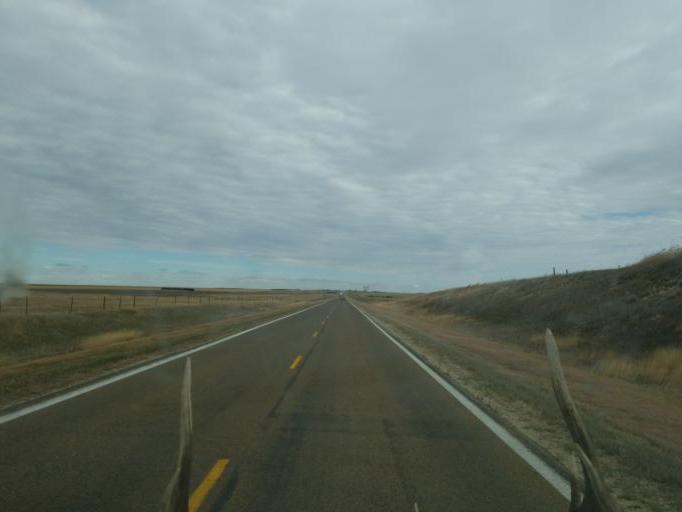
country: US
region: Kansas
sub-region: Logan County
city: Oakley
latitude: 39.0770
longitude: -101.1966
